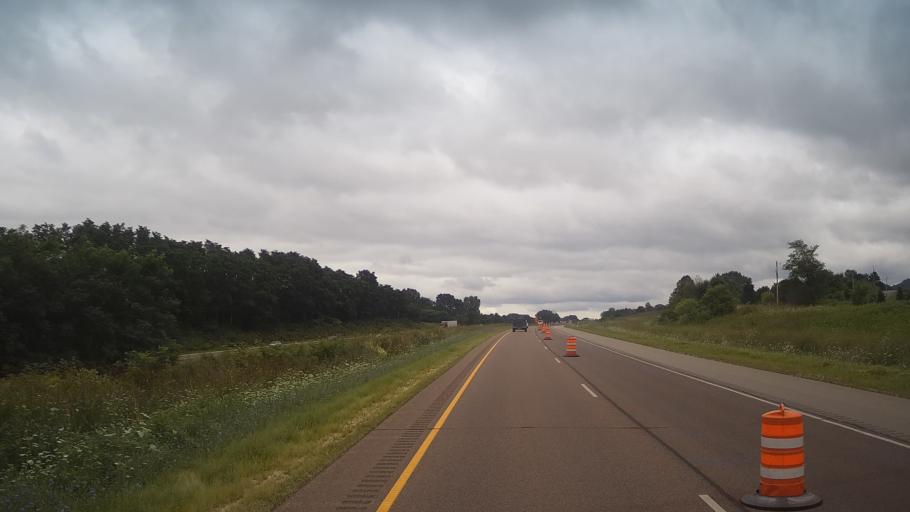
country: US
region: Wisconsin
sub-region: La Crosse County
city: West Salem
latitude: 43.8845
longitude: -91.1111
